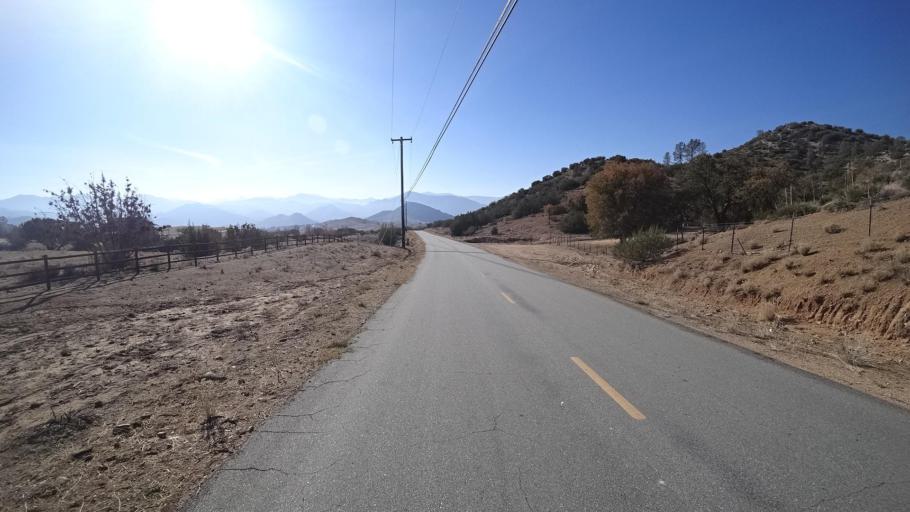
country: US
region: California
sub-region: Kern County
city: Tehachapi
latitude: 35.3589
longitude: -118.3833
